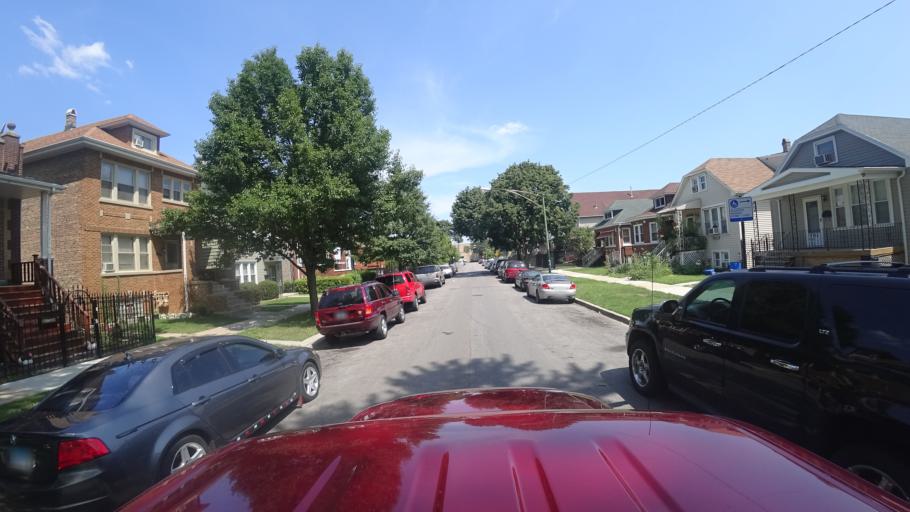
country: US
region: Illinois
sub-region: Cook County
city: Chicago
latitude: 41.7992
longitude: -87.6988
